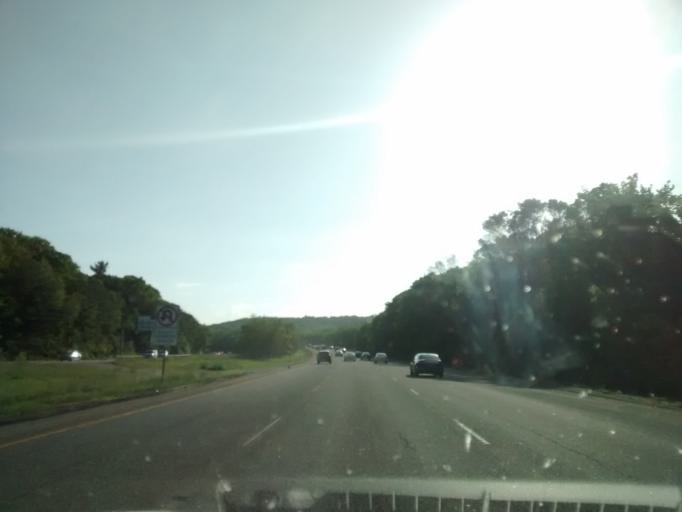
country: US
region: Massachusetts
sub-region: Worcester County
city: Northborough
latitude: 42.3326
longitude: -71.6820
